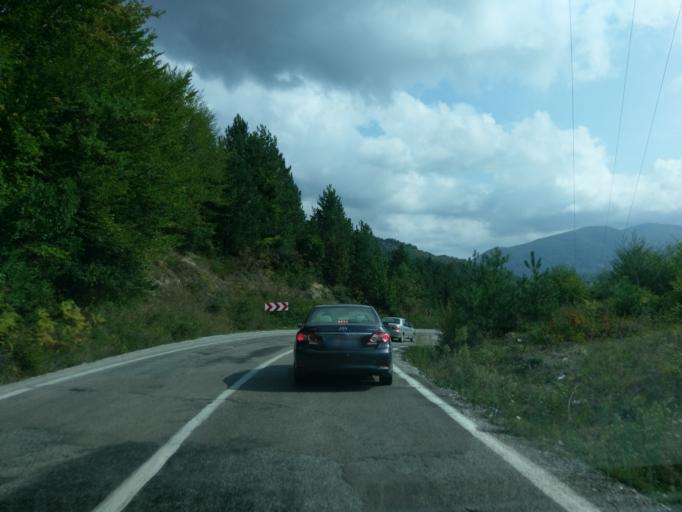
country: TR
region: Sinop
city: Yenikonak
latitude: 41.8765
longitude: 34.5451
